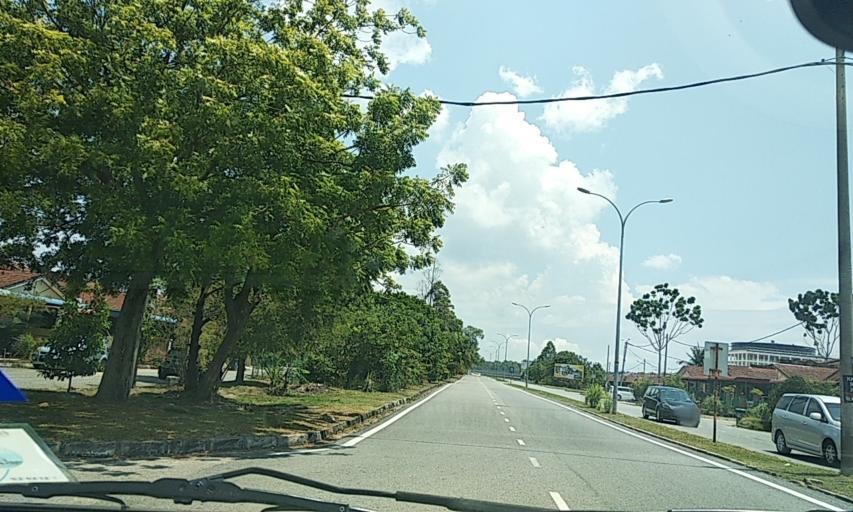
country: MY
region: Kedah
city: Sungai Petani
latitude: 5.6366
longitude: 100.4703
